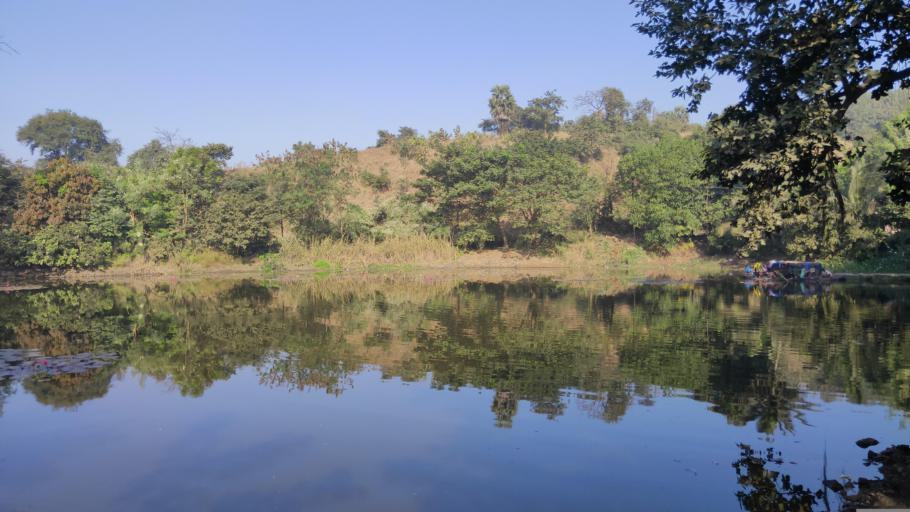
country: IN
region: Maharashtra
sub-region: Thane
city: Bhiwandi
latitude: 19.3117
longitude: 72.9769
